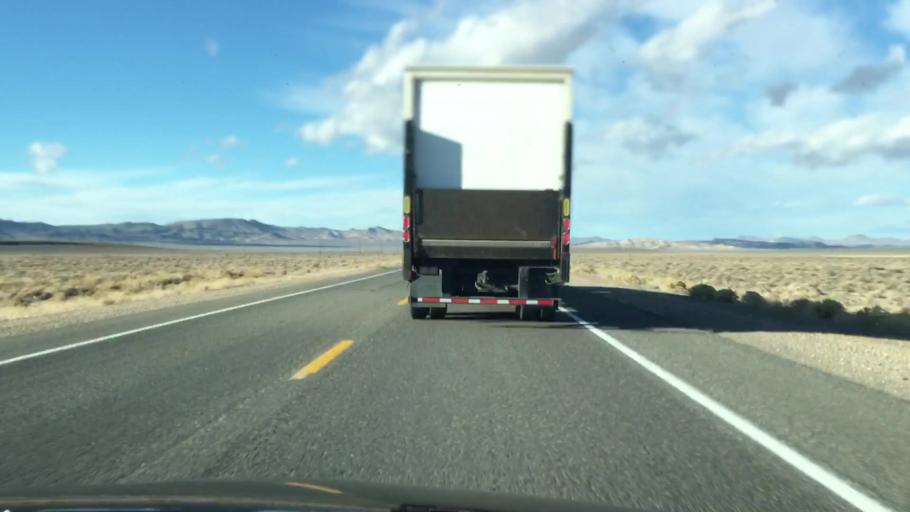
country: US
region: Nevada
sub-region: Esmeralda County
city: Goldfield
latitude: 37.4353
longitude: -117.1622
